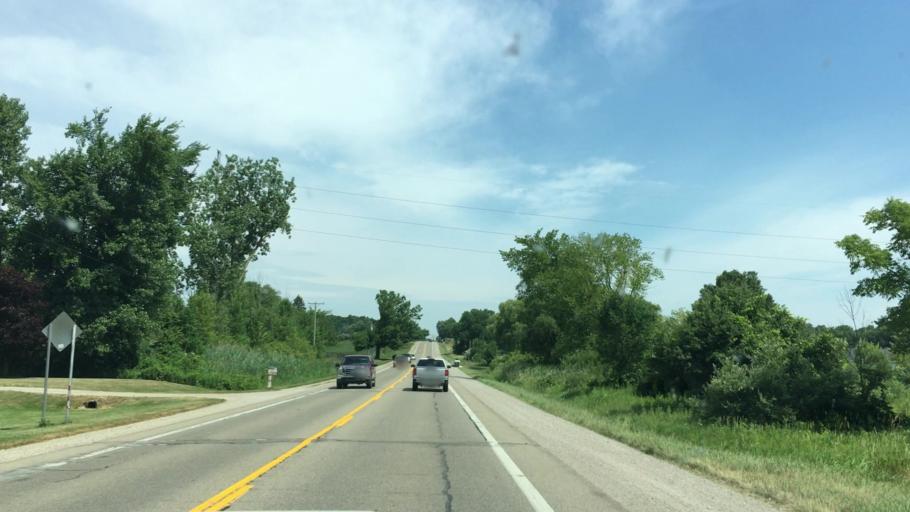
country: US
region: Michigan
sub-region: Lapeer County
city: Imlay City
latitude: 43.0679
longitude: -83.0748
